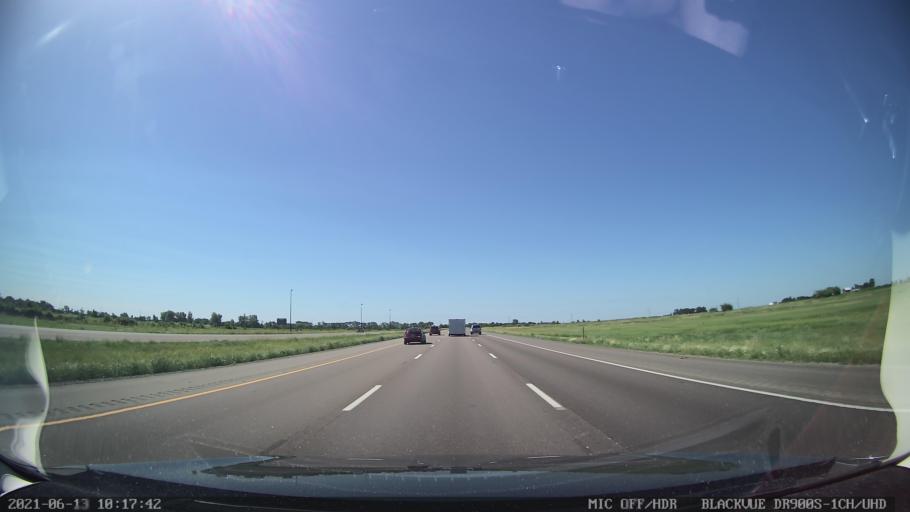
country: US
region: Illinois
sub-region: Logan County
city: Lincoln
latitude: 40.1103
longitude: -89.4171
